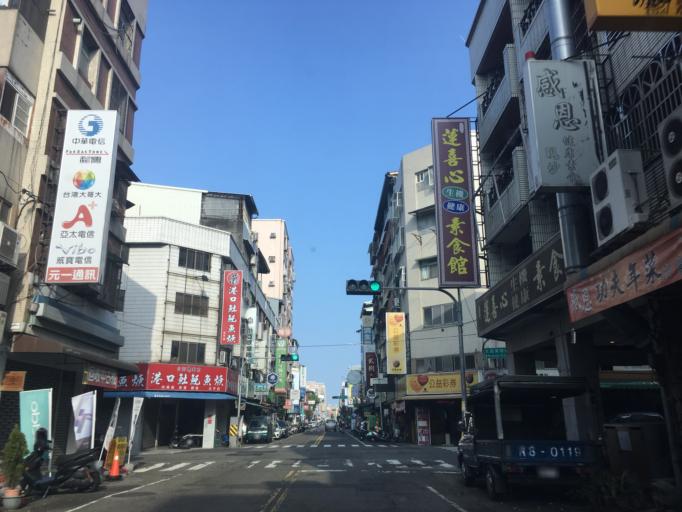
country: TW
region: Taiwan
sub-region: Taichung City
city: Taichung
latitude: 24.1710
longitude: 120.6826
